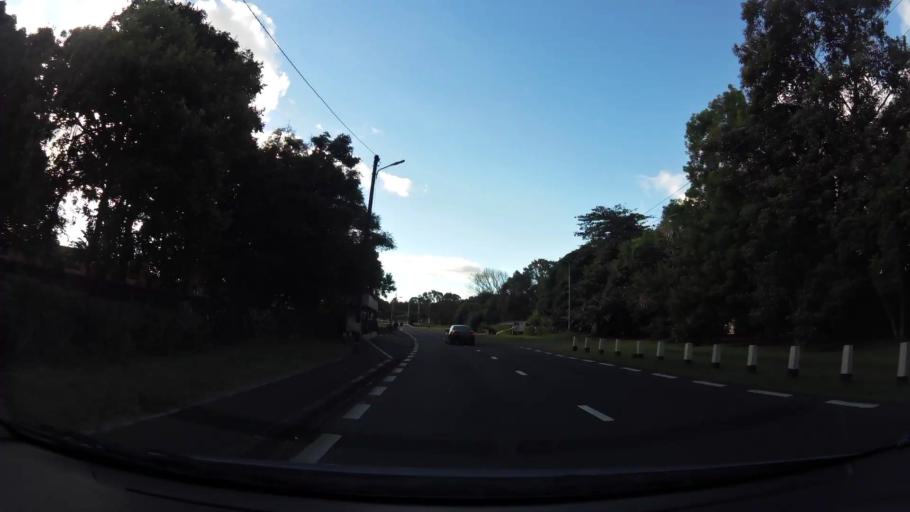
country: MU
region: Plaines Wilhems
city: Vacoas
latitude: -20.2831
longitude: 57.4979
